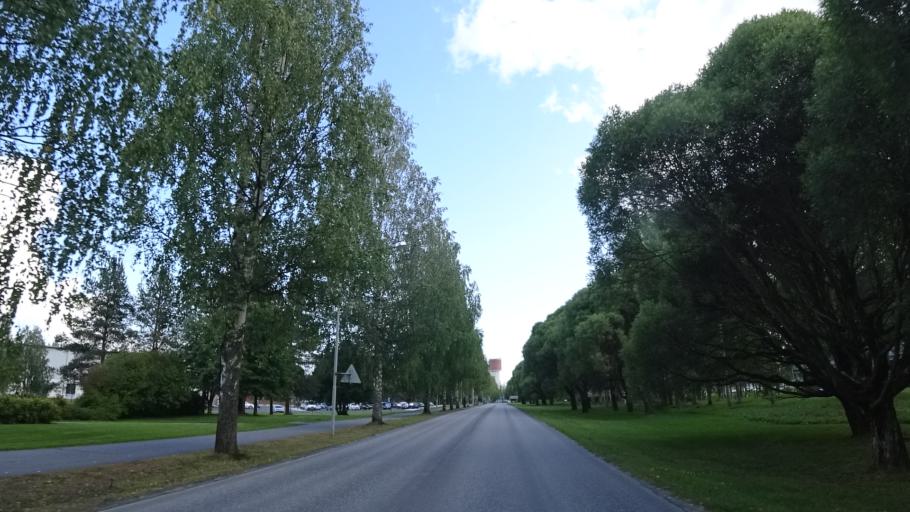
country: FI
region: North Karelia
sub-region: Pielisen Karjala
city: Lieksa
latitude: 63.3267
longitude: 30.0225
